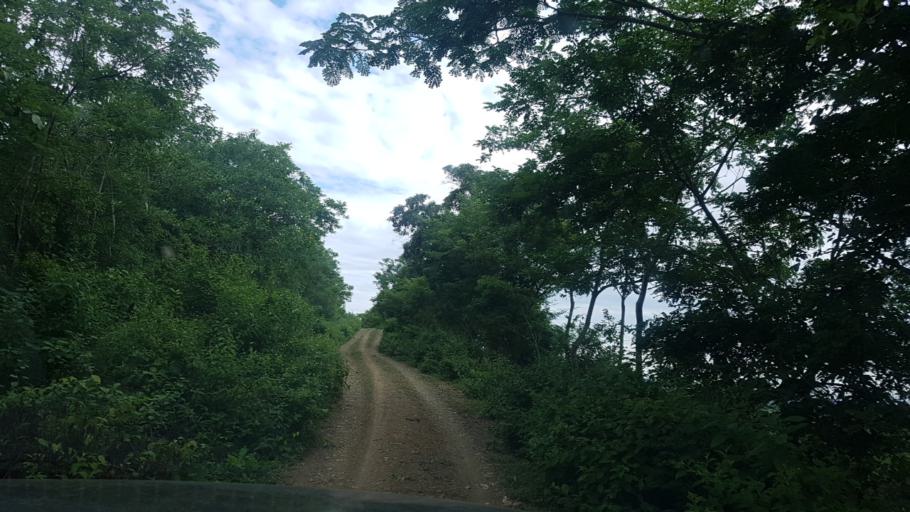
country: NI
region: Nueva Segovia
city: Ciudad Antigua
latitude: 13.5929
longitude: -86.3705
